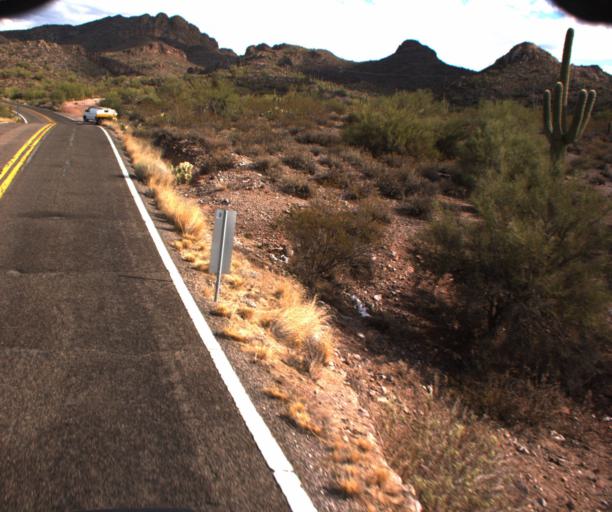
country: US
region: Arizona
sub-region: Pinal County
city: Apache Junction
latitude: 33.4968
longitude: -111.4643
